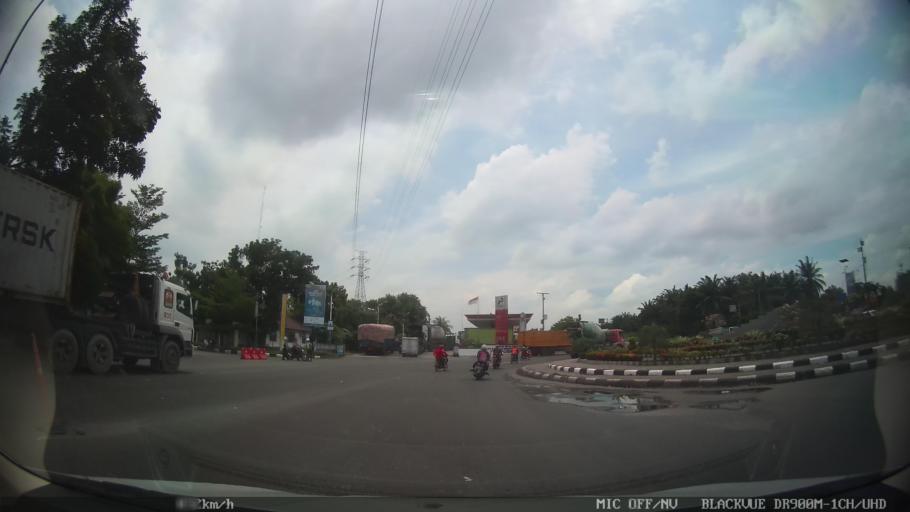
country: ID
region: North Sumatra
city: Labuhan Deli
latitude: 3.6728
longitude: 98.6833
